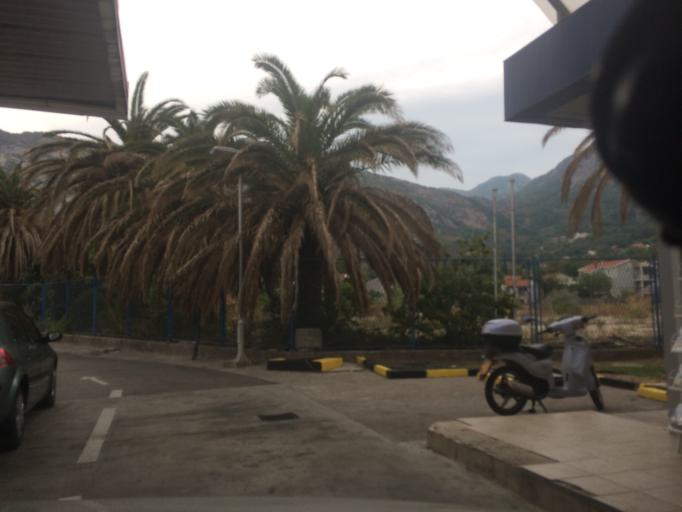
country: ME
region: Kotor
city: Risan
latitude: 42.5109
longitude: 18.6962
